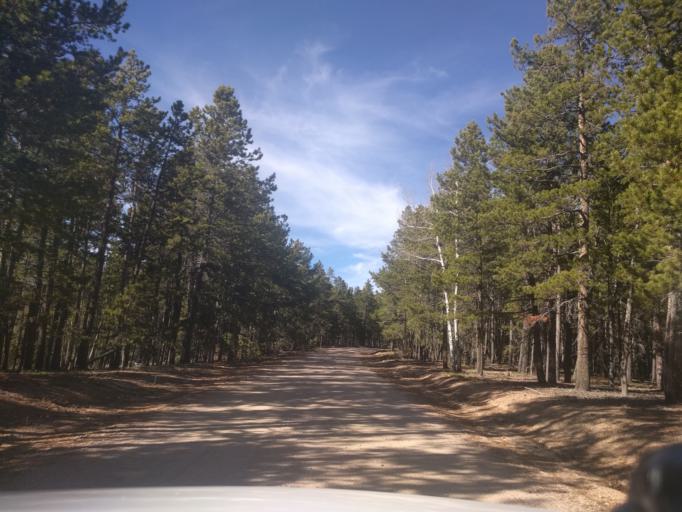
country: US
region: Colorado
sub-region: Douglas County
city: Perry Park
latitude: 39.1911
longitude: -105.0514
